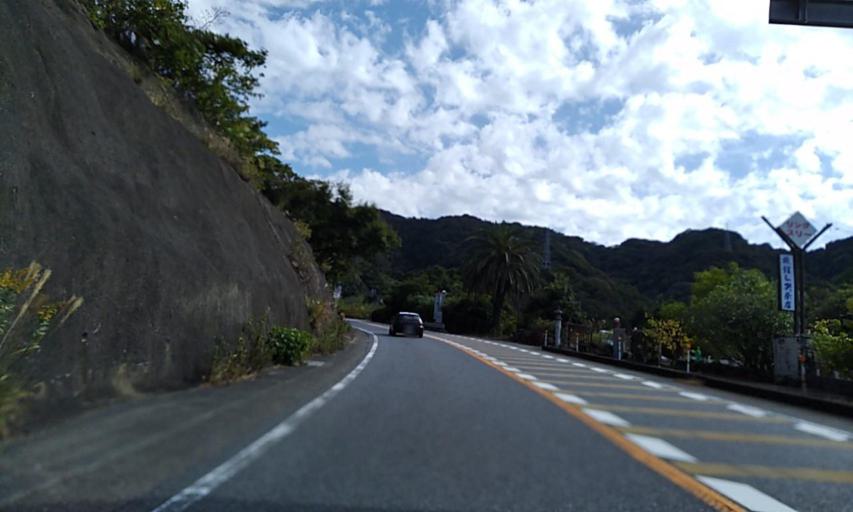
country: JP
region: Wakayama
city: Gobo
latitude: 33.9547
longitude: 135.1227
